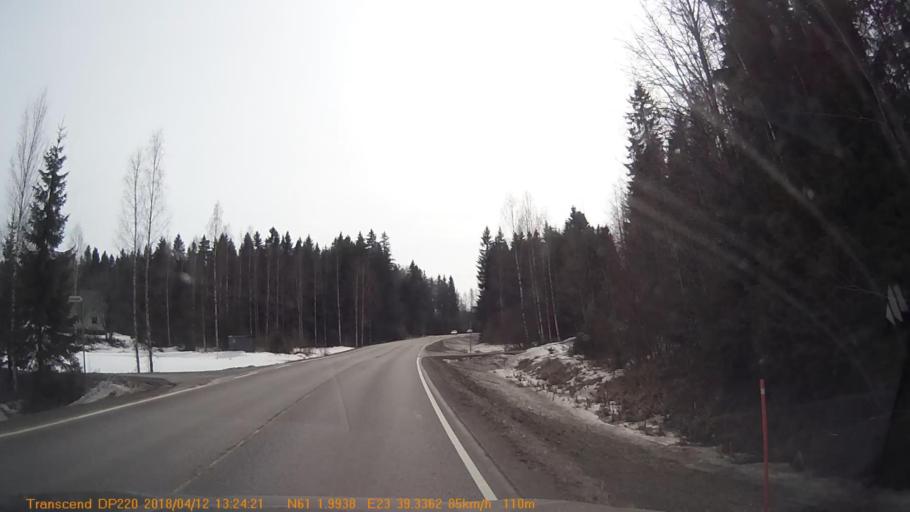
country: FI
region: Pirkanmaa
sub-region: Etelae-Pirkanmaa
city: Kylmaekoski
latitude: 61.0320
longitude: 23.6557
